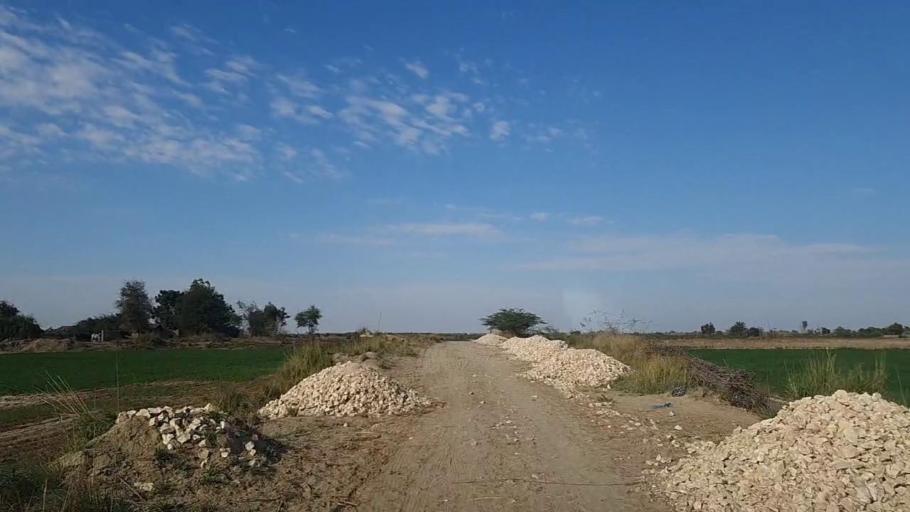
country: PK
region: Sindh
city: Jam Sahib
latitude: 26.3159
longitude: 68.8081
